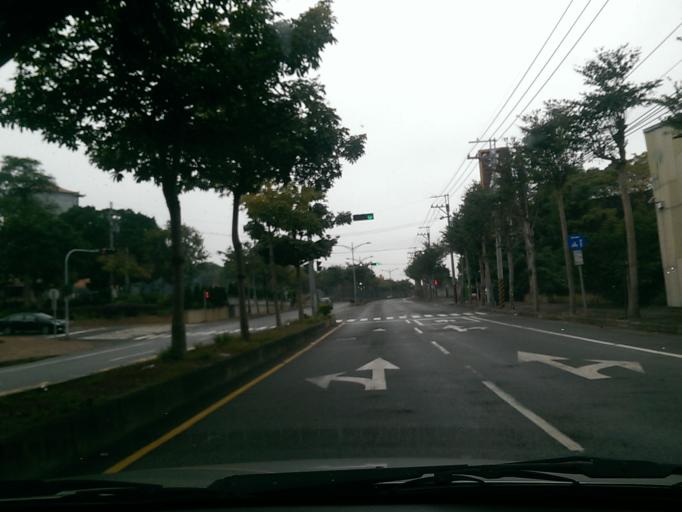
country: TW
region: Taiwan
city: Fengyuan
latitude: 24.2267
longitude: 120.6136
